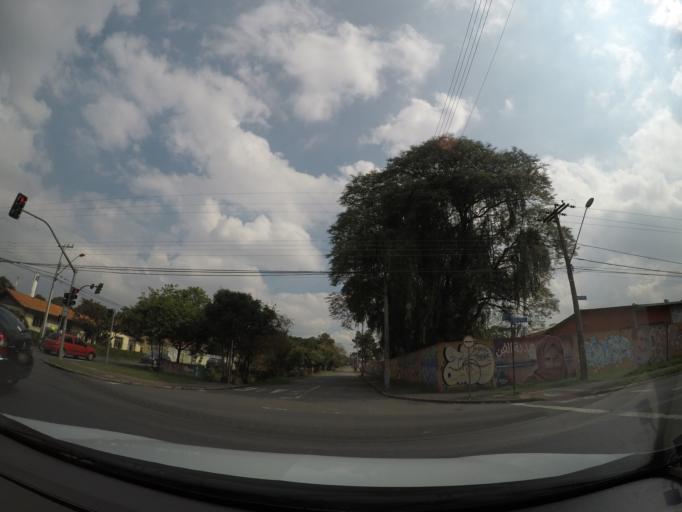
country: BR
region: Parana
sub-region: Sao Jose Dos Pinhais
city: Sao Jose dos Pinhais
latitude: -25.4960
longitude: -49.2415
